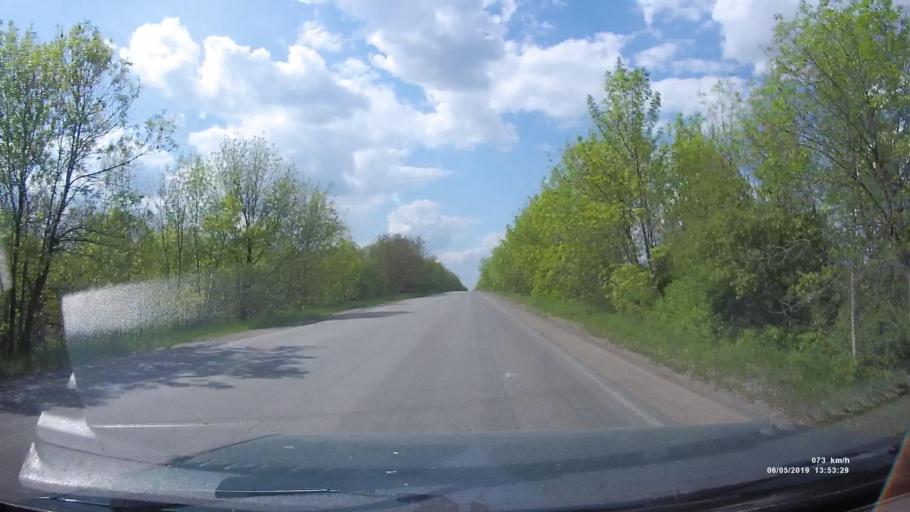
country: RU
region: Rostov
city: Melikhovskaya
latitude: 47.6686
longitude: 40.4615
